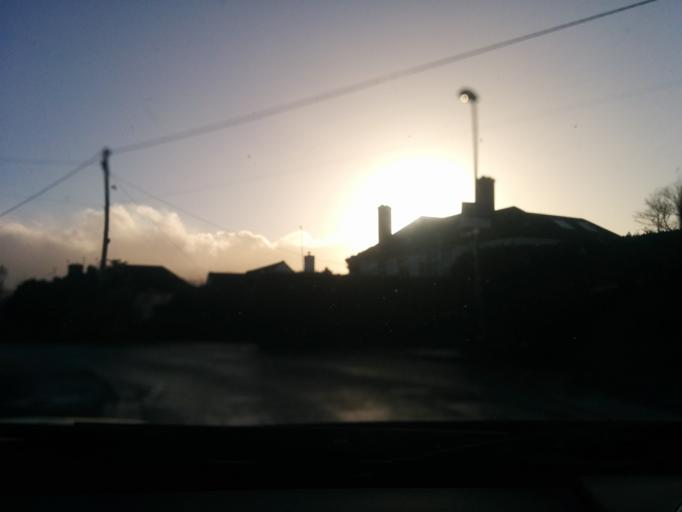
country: GB
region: England
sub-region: Oxfordshire
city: Abingdon
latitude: 51.6750
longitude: -1.2945
